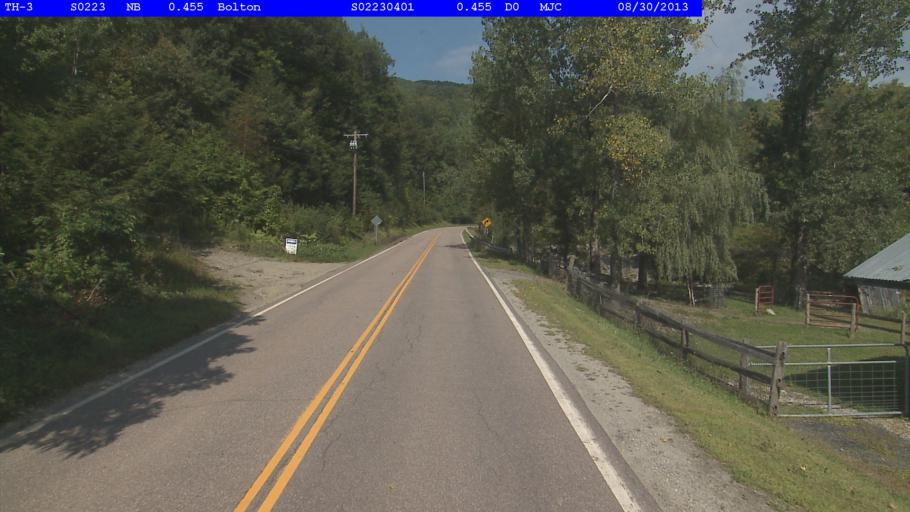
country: US
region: Vermont
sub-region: Washington County
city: Waterbury
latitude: 44.3781
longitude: -72.8750
